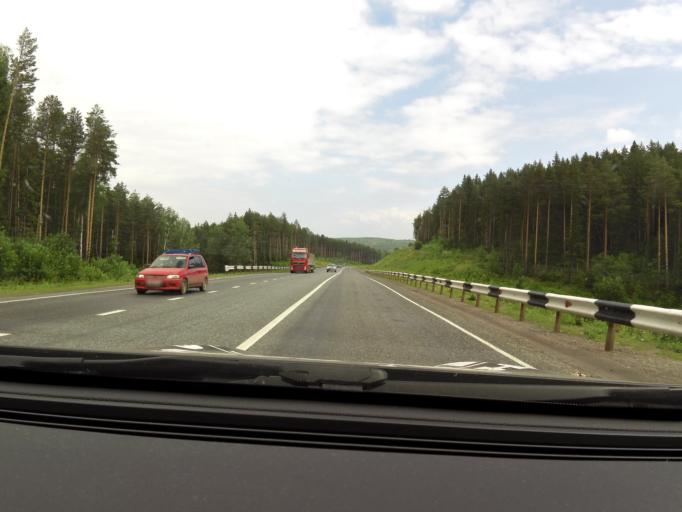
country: RU
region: Perm
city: Suksun
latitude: 57.0934
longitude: 57.3399
